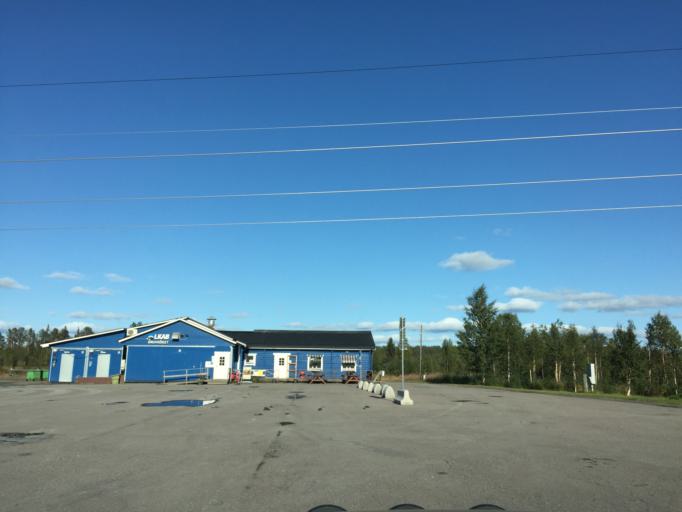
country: SE
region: Norrbotten
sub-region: Gallivare Kommun
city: Malmberget
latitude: 67.6522
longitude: 21.0175
